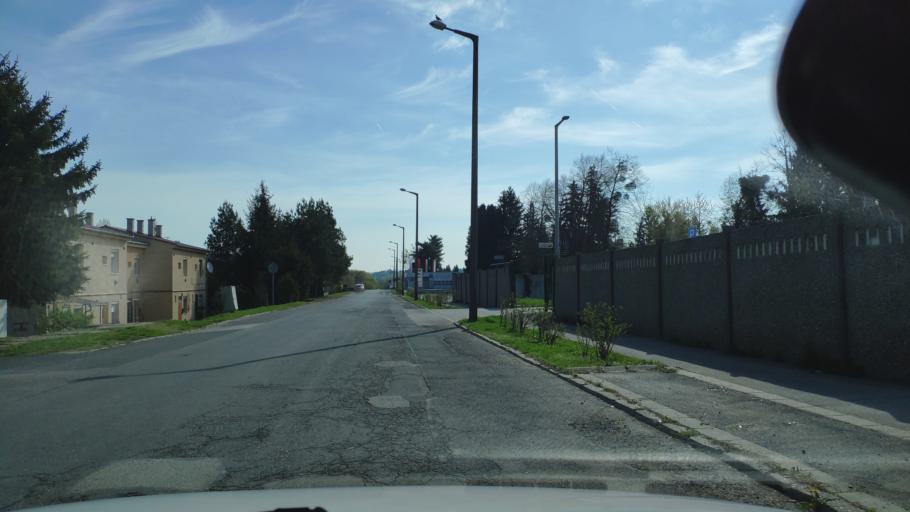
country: HU
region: Zala
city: Nagykanizsa
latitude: 46.4432
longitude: 16.9983
